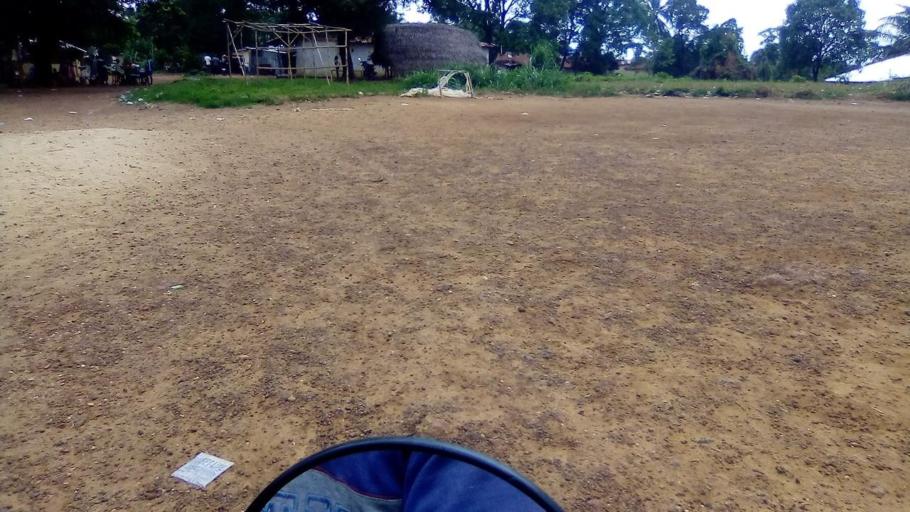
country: SL
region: Southern Province
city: Bo
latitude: 7.9612
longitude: -11.7228
